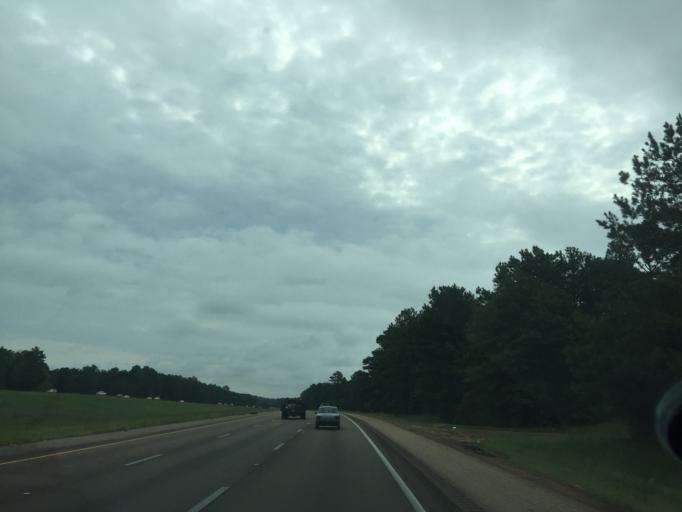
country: US
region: Mississippi
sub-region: Rankin County
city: Pearl
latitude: 32.2657
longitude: -90.1037
